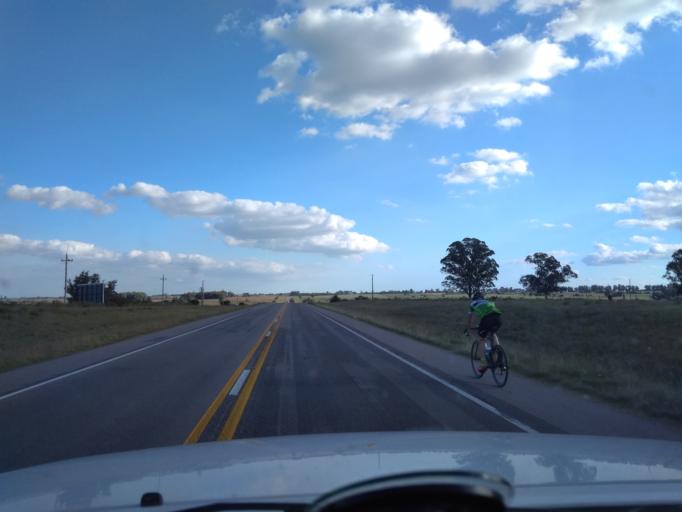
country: UY
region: Florida
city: Florida
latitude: -34.2118
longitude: -56.2058
